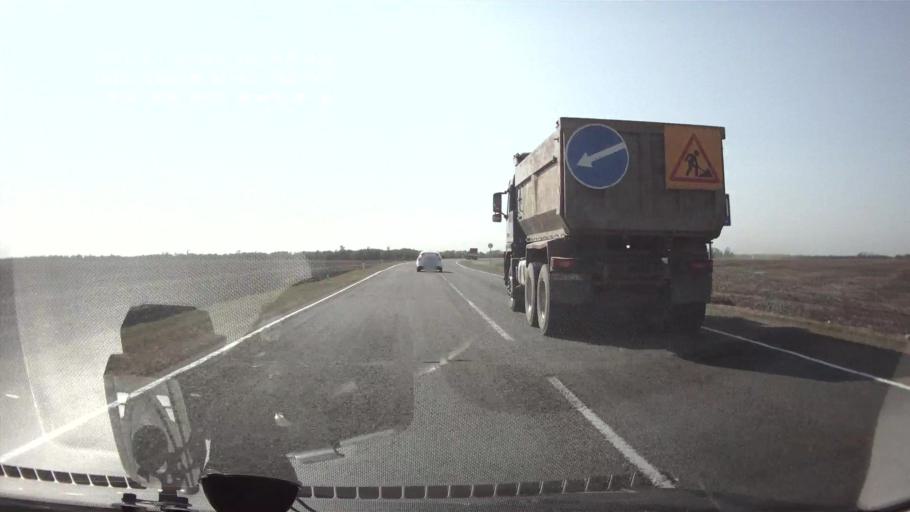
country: RU
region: Krasnodarskiy
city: Belaya Glina
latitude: 46.0162
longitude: 40.7989
